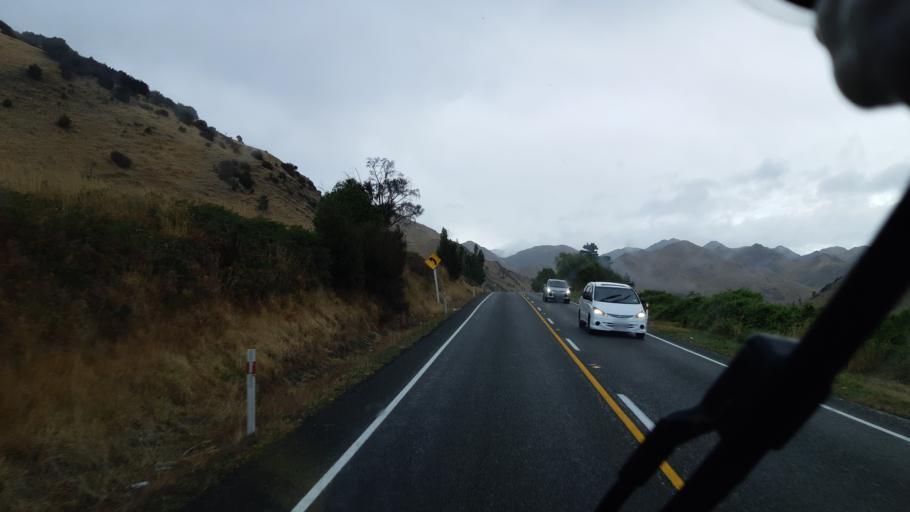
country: NZ
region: Canterbury
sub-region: Hurunui District
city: Amberley
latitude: -42.6720
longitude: 172.7746
